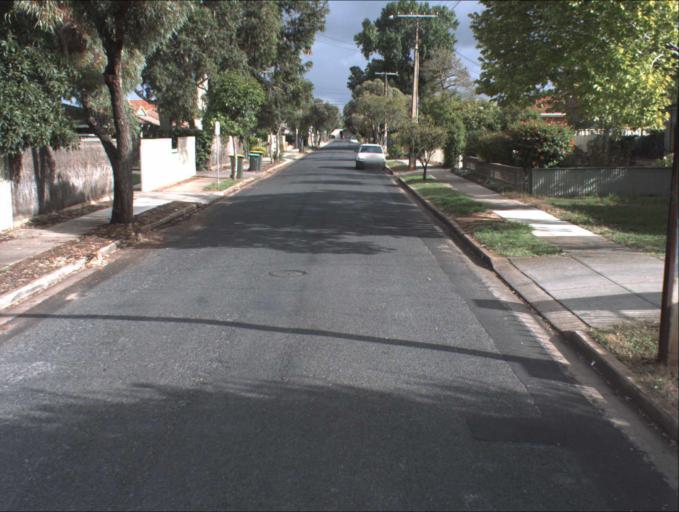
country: AU
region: South Australia
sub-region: Port Adelaide Enfield
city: Klemzig
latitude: -34.8810
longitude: 138.6373
